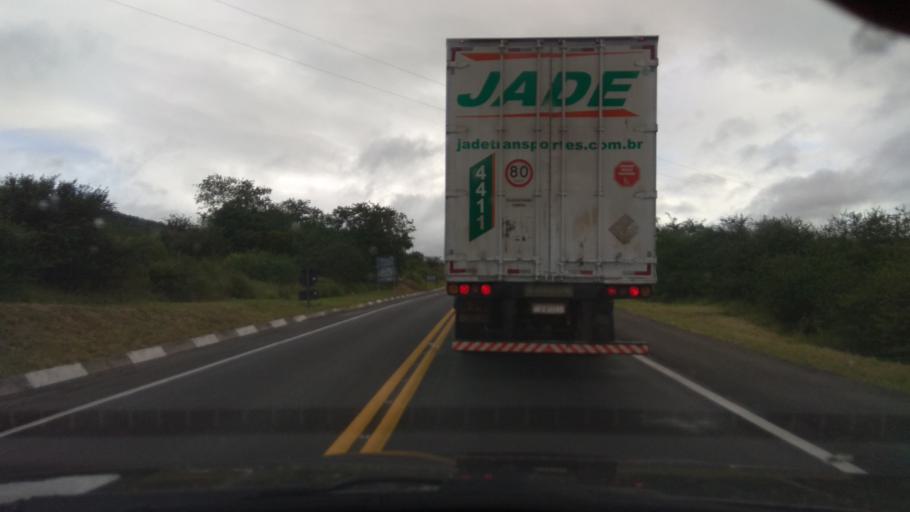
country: BR
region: Bahia
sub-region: Santa Ines
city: Santa Ines
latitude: -13.2769
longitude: -40.0152
